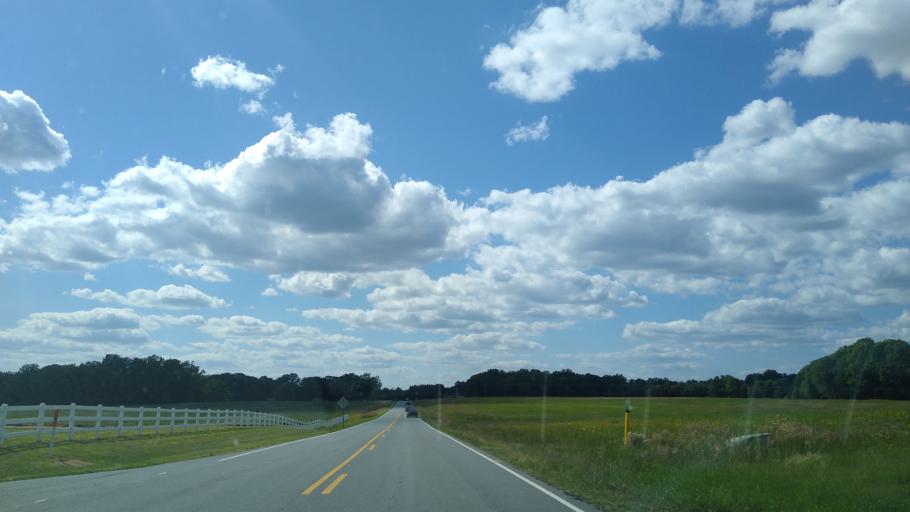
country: US
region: North Carolina
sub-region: Forsyth County
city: Kernersville
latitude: 36.0975
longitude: -80.0762
